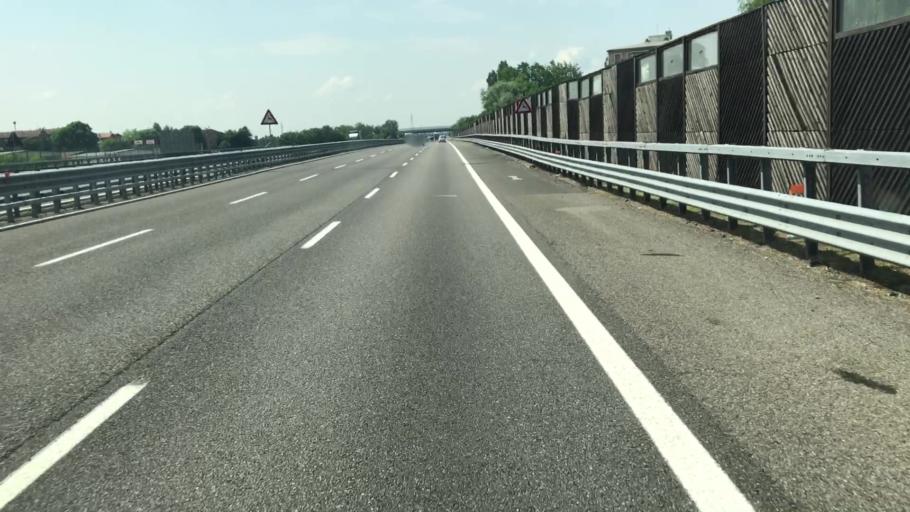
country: IT
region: Lombardy
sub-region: Citta metropolitana di Milano
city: Binasco
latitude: 45.3339
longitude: 9.0938
